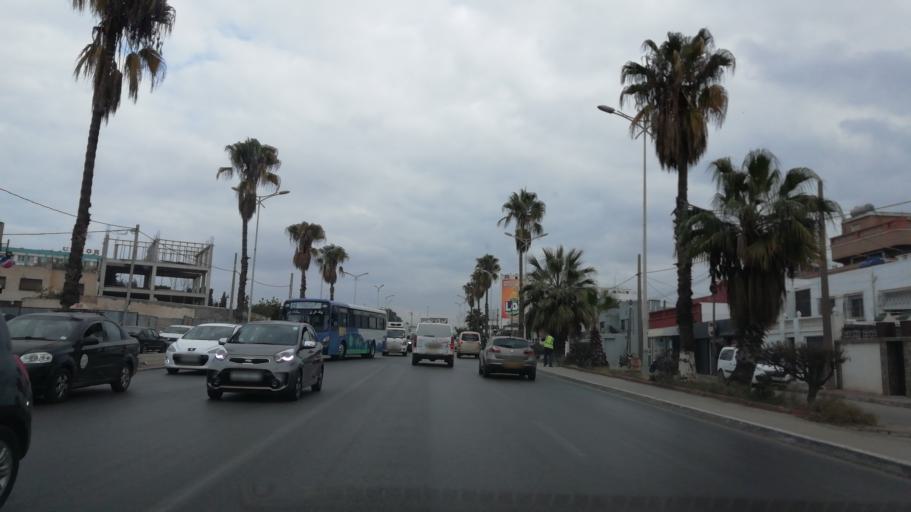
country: DZ
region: Oran
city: Oran
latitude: 35.6954
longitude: -0.6151
